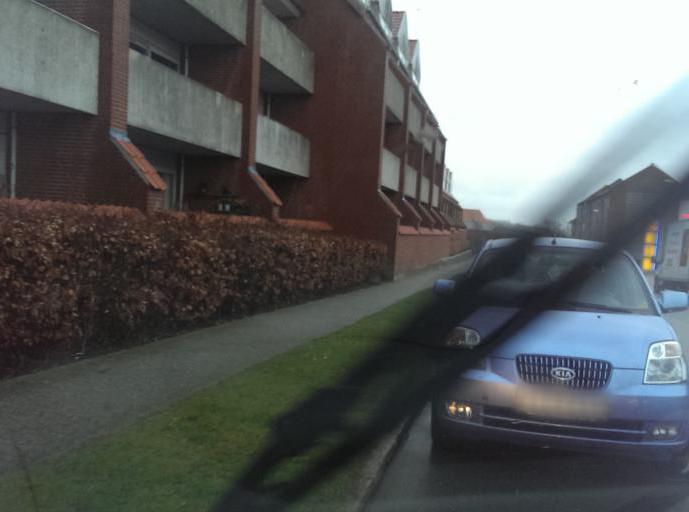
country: DK
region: South Denmark
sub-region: Esbjerg Kommune
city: Esbjerg
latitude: 55.4645
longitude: 8.4600
